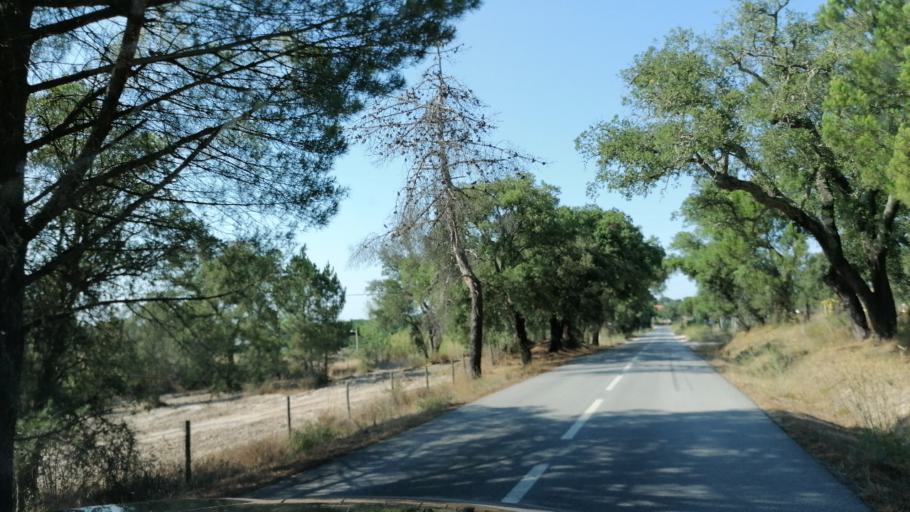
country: PT
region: Santarem
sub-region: Benavente
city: Poceirao
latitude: 38.7580
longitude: -8.6325
